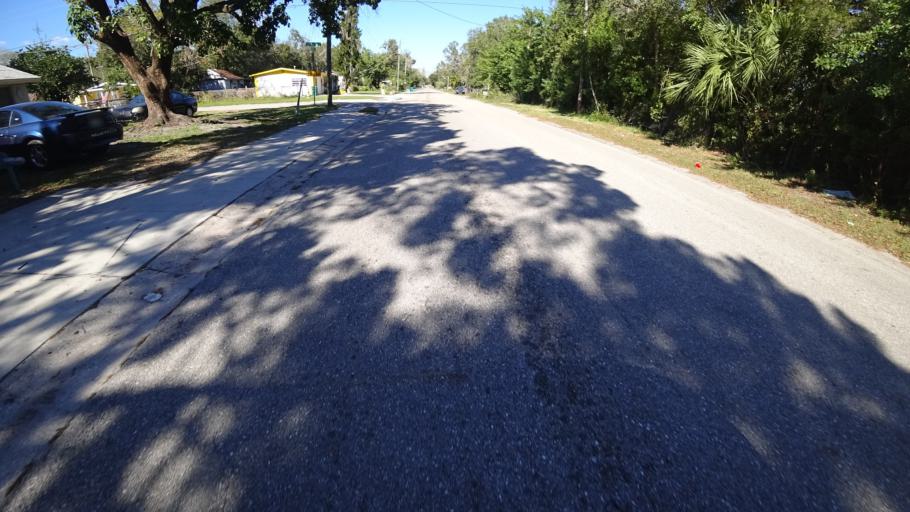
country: US
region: Florida
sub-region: Manatee County
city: Whitfield
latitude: 27.4350
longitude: -82.5524
